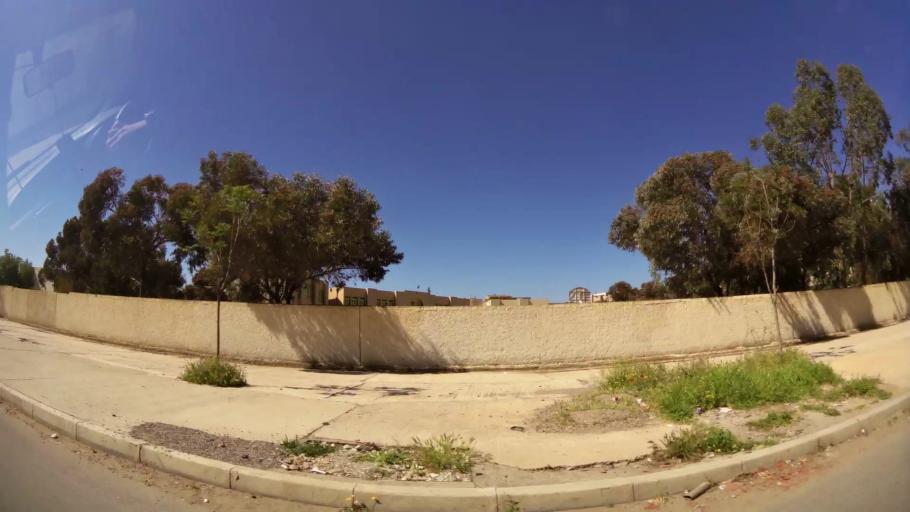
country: MA
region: Oriental
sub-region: Oujda-Angad
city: Oujda
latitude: 34.6563
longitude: -1.9335
